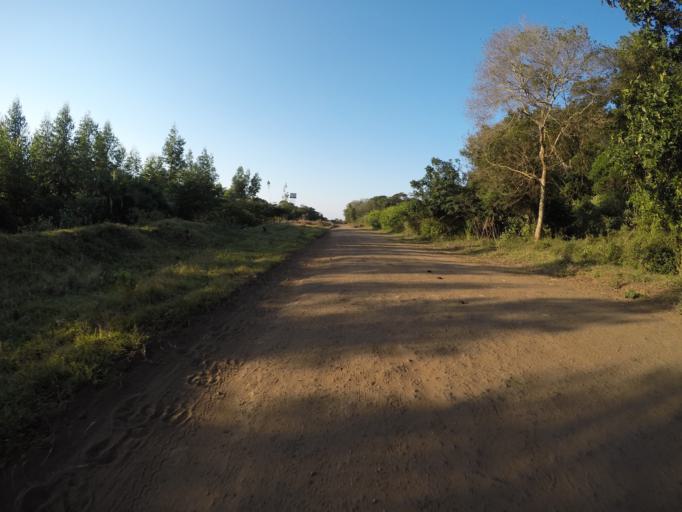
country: ZA
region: KwaZulu-Natal
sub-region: uThungulu District Municipality
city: KwaMbonambi
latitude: -28.6956
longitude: 32.1968
